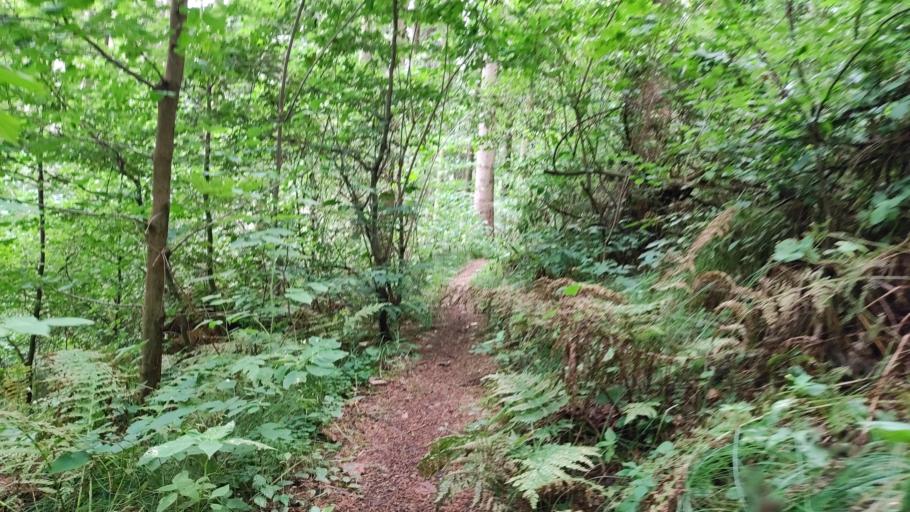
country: DE
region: Bavaria
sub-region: Swabia
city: Jettingen-Scheppach
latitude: 48.3733
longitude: 10.4042
